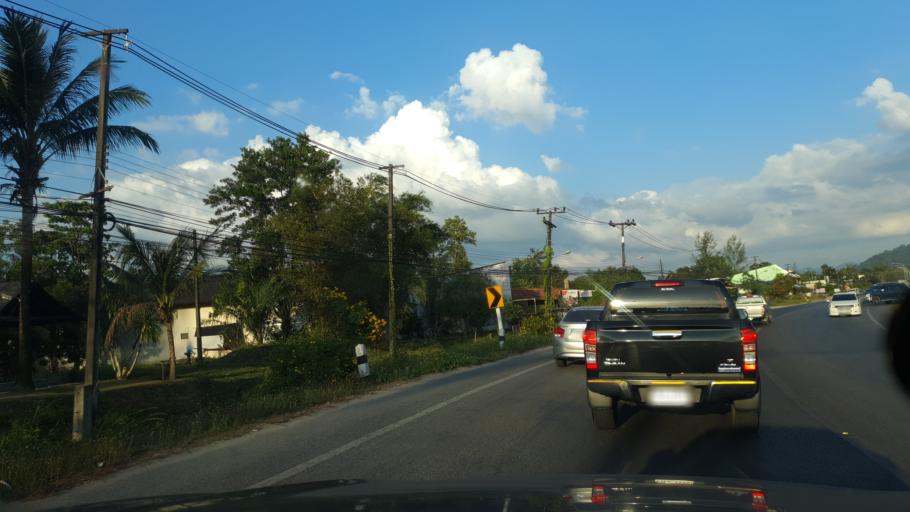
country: TH
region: Phangnga
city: Takua Pa
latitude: 8.8452
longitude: 98.2901
